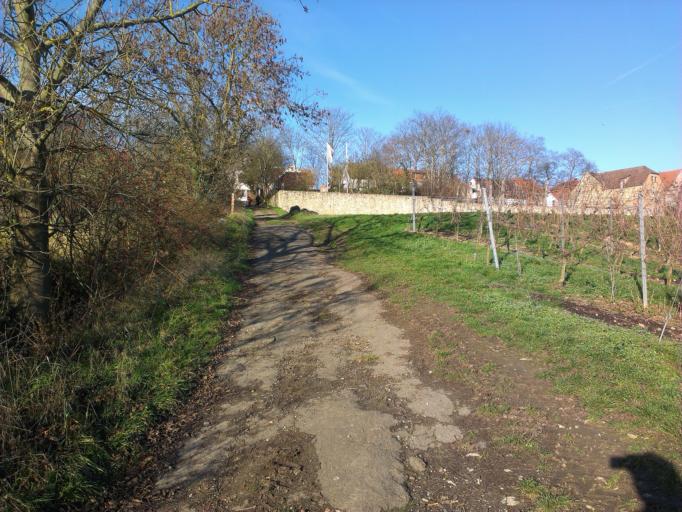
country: DE
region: Rheinland-Pfalz
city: Molsheim
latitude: 49.6443
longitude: 8.1644
